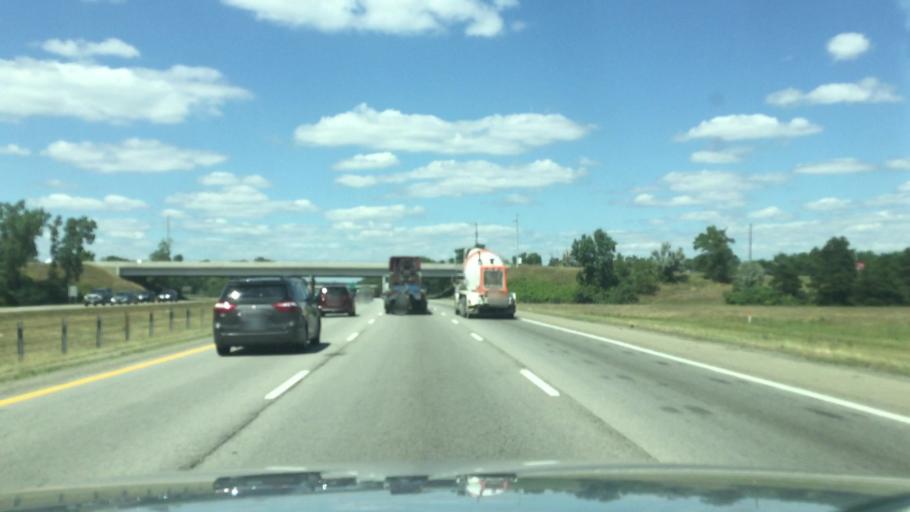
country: US
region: Michigan
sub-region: Wayne County
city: Plymouth
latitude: 42.3576
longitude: -83.4358
